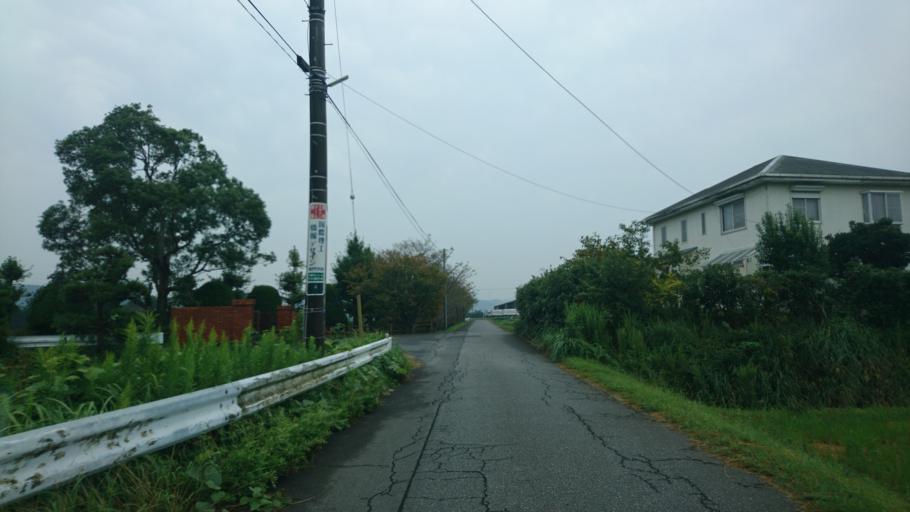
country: JP
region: Chiba
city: Kimitsu
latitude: 35.3076
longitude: 139.9598
